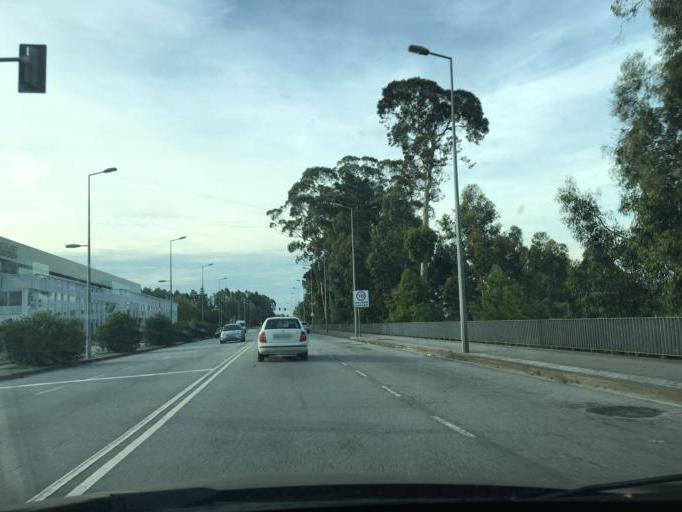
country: PT
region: Porto
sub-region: Maia
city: Maia
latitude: 41.2366
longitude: -8.6418
